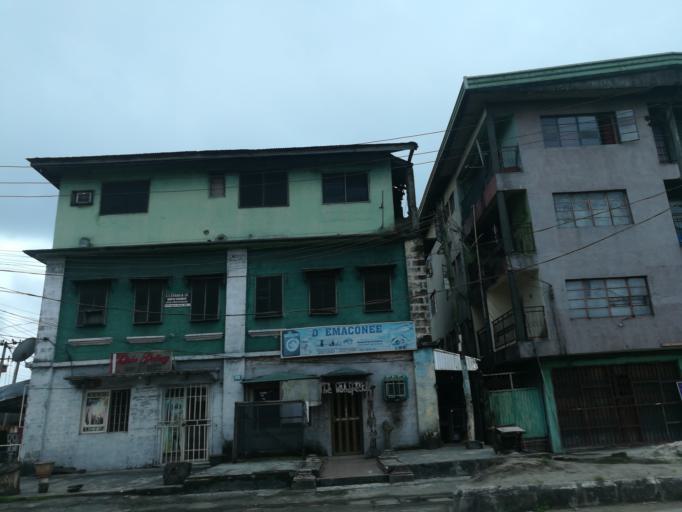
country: NG
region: Rivers
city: Port Harcourt
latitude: 4.7619
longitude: 7.0265
